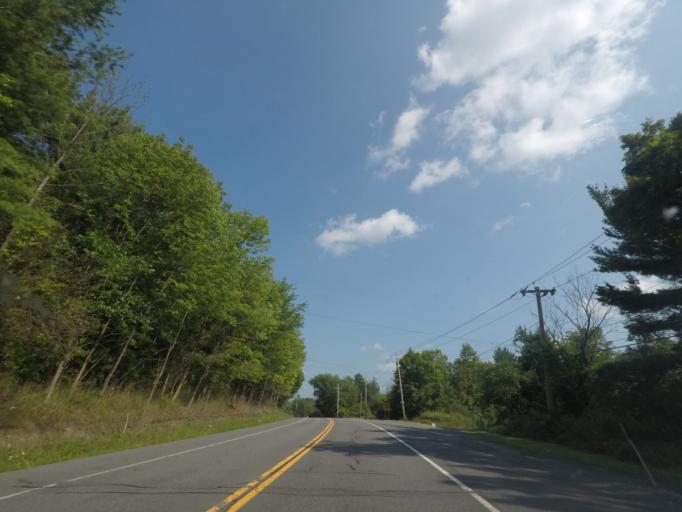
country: US
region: New York
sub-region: Rensselaer County
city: Nassau
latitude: 42.5298
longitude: -73.6553
